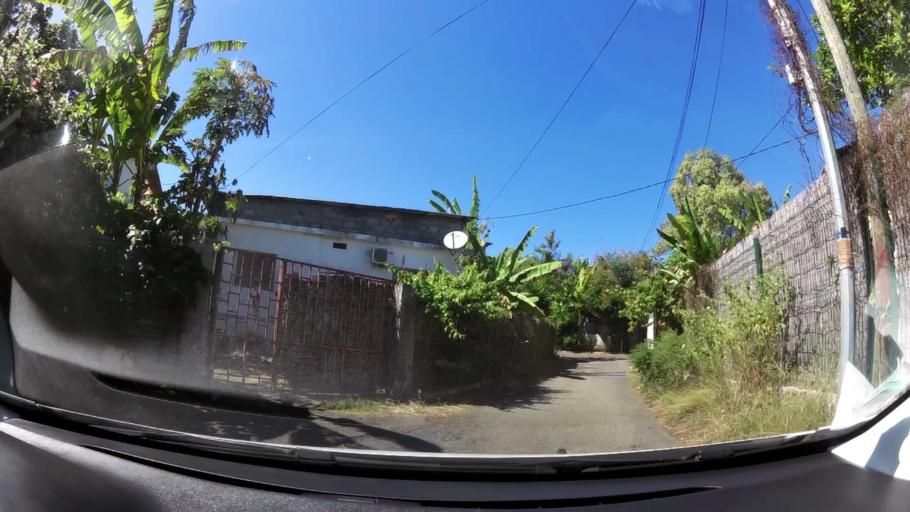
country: YT
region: Pamandzi
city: Pamandzi
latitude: -12.7960
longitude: 45.2825
